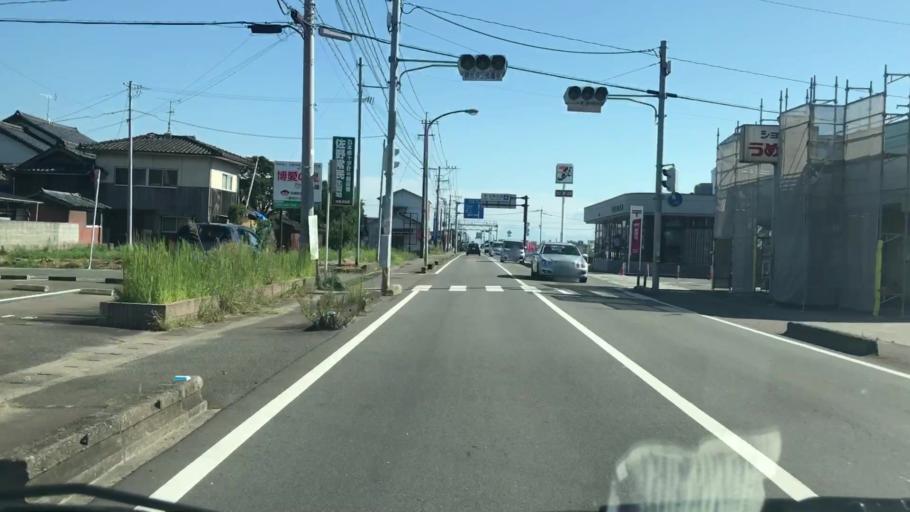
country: JP
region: Saga Prefecture
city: Okawa
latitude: 33.2066
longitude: 130.3353
